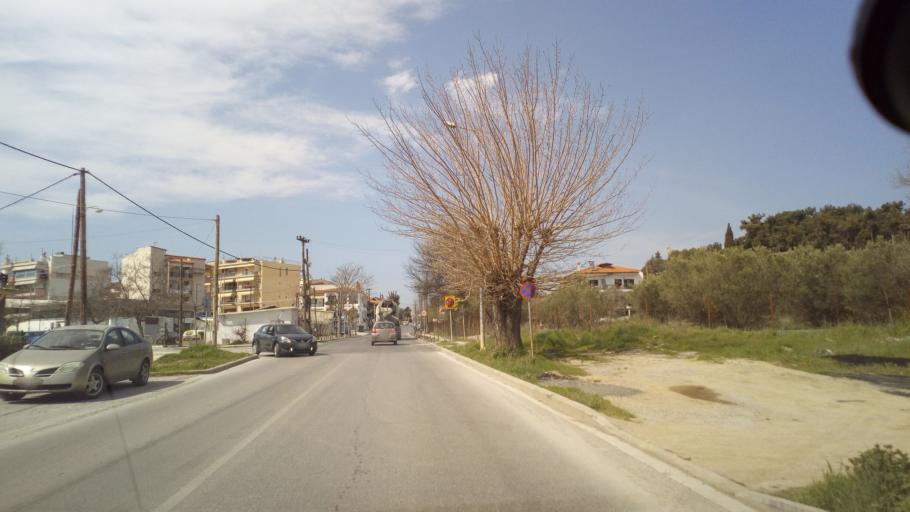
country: GR
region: Central Macedonia
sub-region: Nomos Thessalonikis
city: Thermi
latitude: 40.5466
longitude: 23.0273
